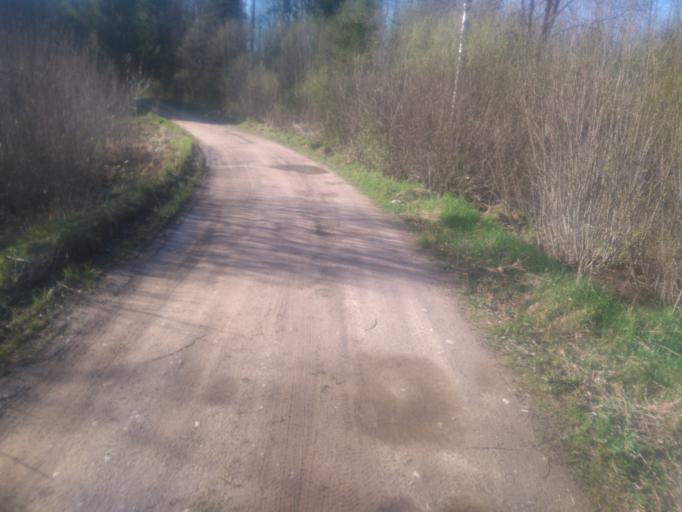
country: LV
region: Vecpiebalga
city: Vecpiebalga
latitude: 57.0062
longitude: 25.8536
